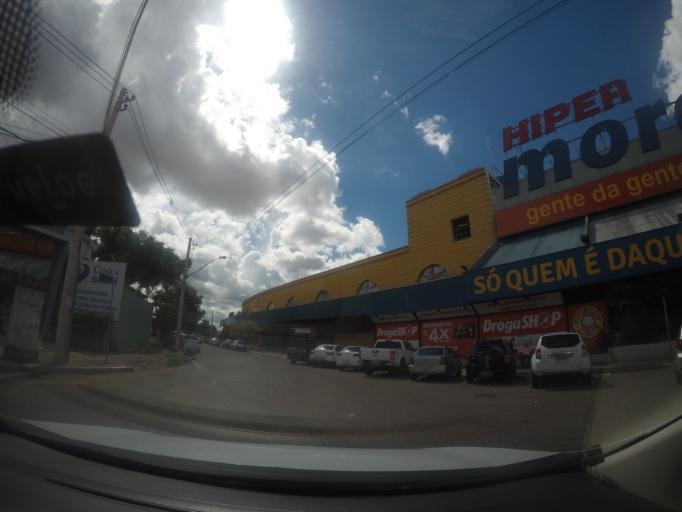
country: BR
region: Goias
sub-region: Goiania
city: Goiania
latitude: -16.6874
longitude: -49.2820
